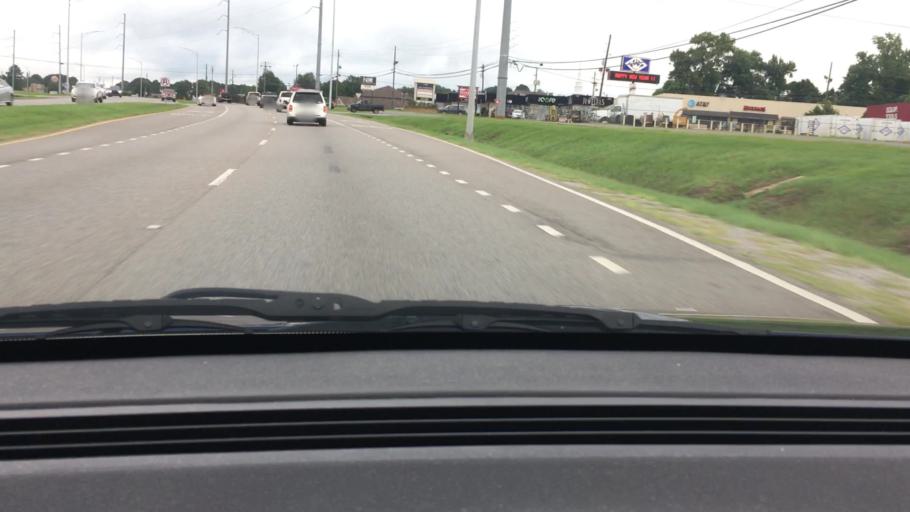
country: US
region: Alabama
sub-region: Tuscaloosa County
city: Tuscaloosa
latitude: 33.2297
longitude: -87.5340
